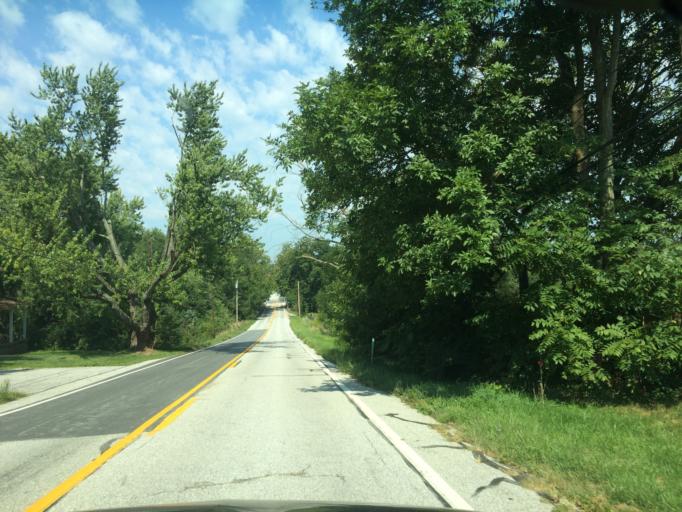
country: US
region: Maryland
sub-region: Carroll County
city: Taneytown
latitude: 39.6392
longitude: -77.1359
